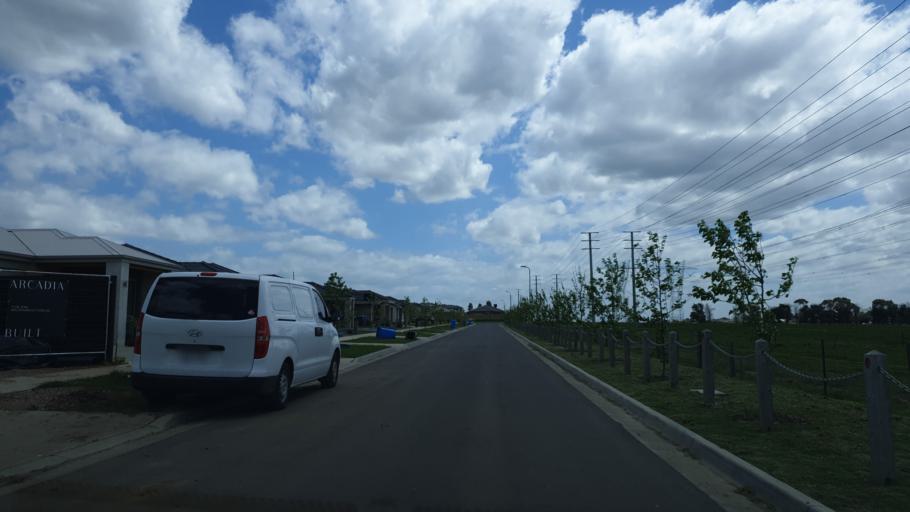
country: AU
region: Victoria
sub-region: Casey
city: Cranbourne
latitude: -38.0923
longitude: 145.2993
